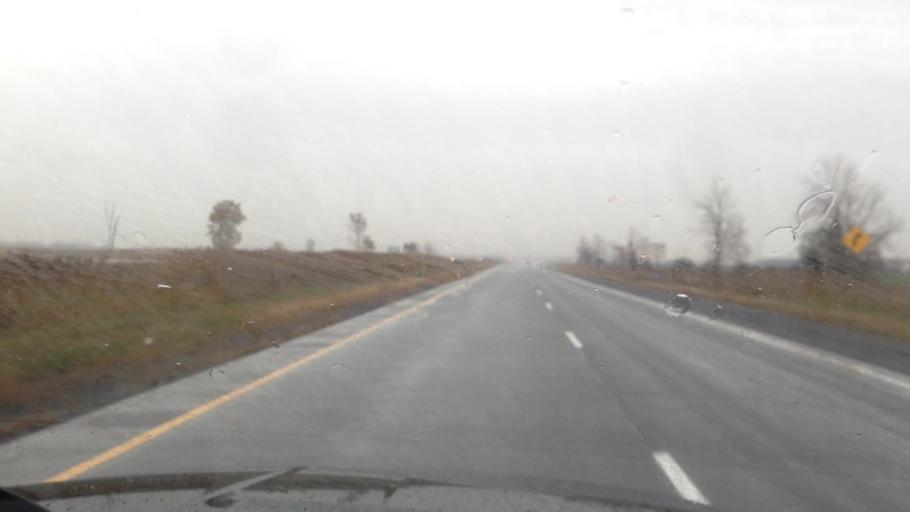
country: CA
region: Ontario
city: Casselman
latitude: 45.3278
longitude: -74.9740
